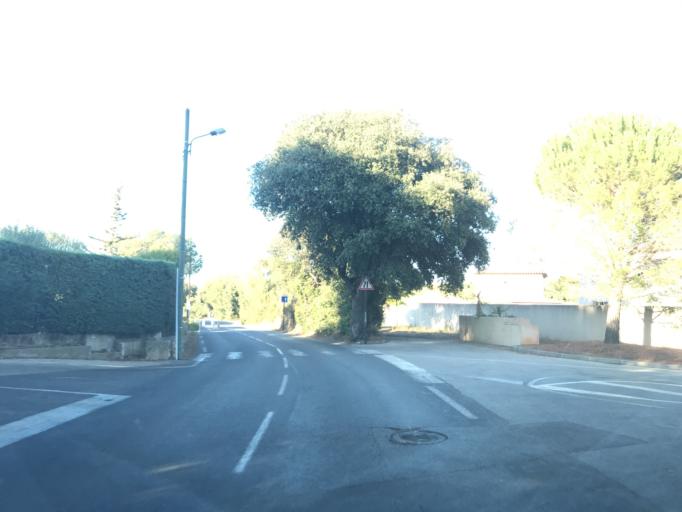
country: FR
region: Provence-Alpes-Cote d'Azur
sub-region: Departement du Var
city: Six-Fours-les-Plages
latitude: 43.0746
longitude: 5.8577
